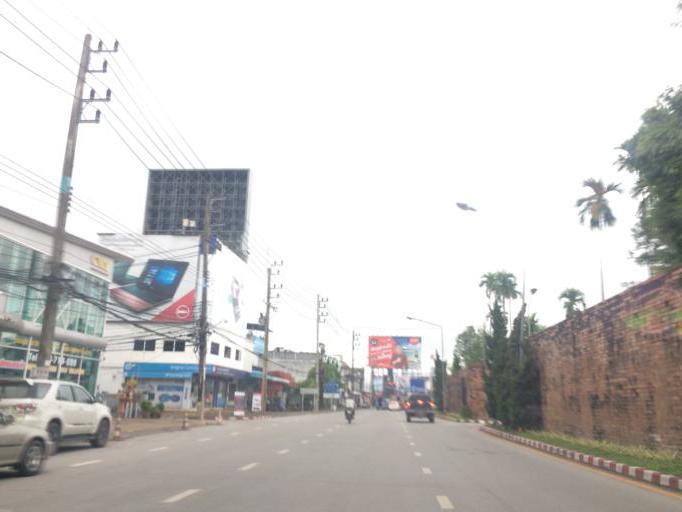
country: TH
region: Chiang Rai
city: Chiang Rai
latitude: 19.9088
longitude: 99.8404
